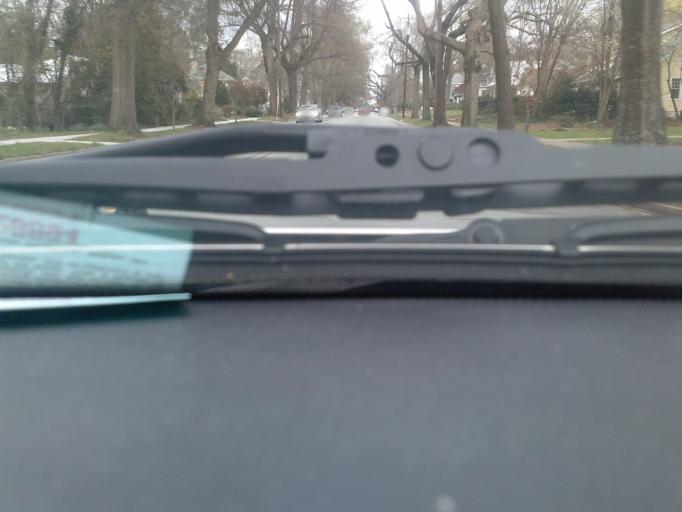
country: US
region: North Carolina
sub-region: Durham County
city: Durham
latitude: 36.0174
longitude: -78.9254
